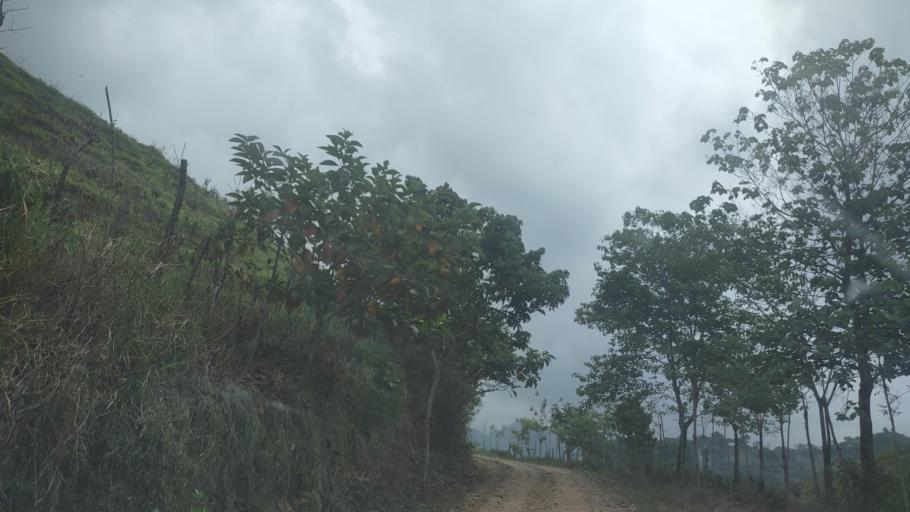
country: MX
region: Tabasco
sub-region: Huimanguillo
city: Francisco Rueda
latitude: 17.4411
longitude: -94.0282
